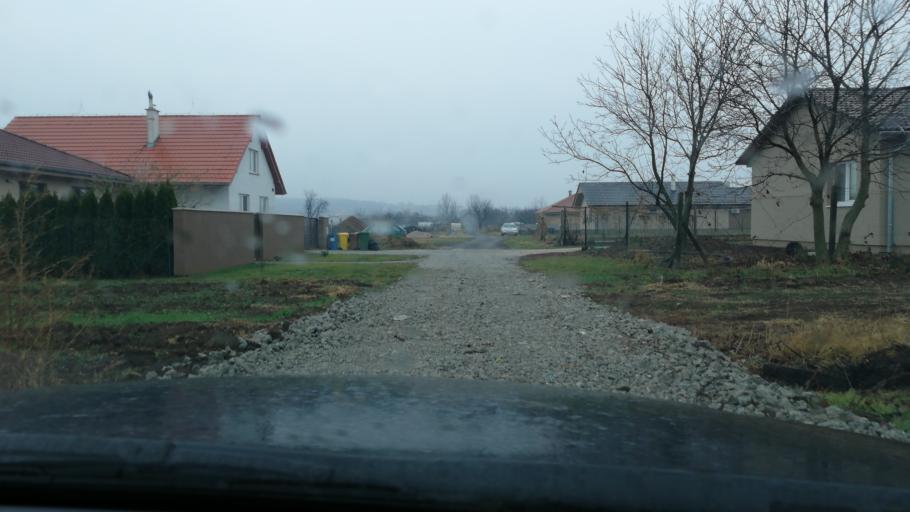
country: SK
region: Nitriansky
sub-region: Okres Nitra
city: Nitra
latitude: 48.3163
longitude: 17.9860
